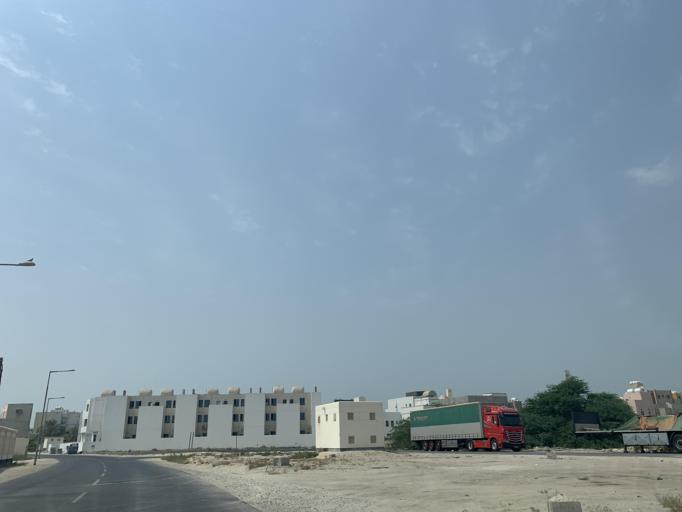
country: BH
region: Manama
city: Jidd Hafs
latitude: 26.2092
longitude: 50.4863
